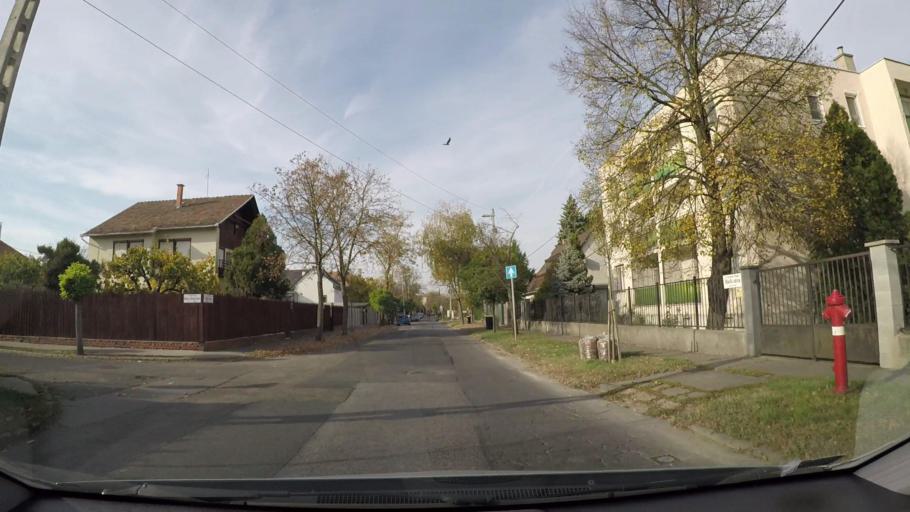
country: HU
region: Budapest
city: Budapest X. keruelet
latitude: 47.4775
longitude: 19.1581
